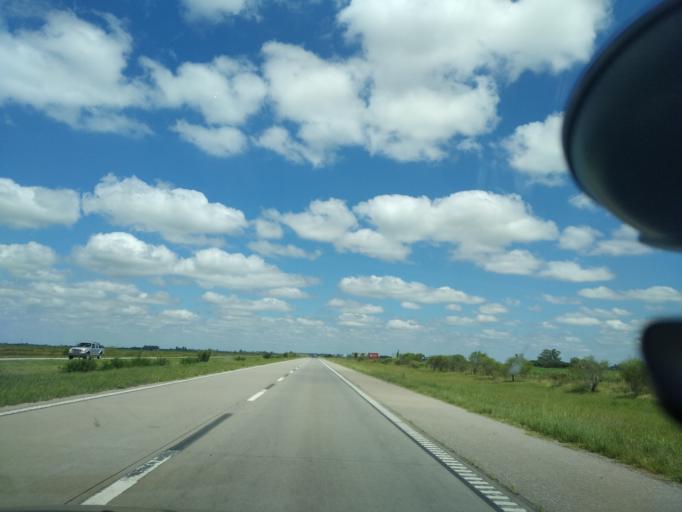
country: AR
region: Cordoba
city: Tio Pujio
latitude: -32.3192
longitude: -63.2738
